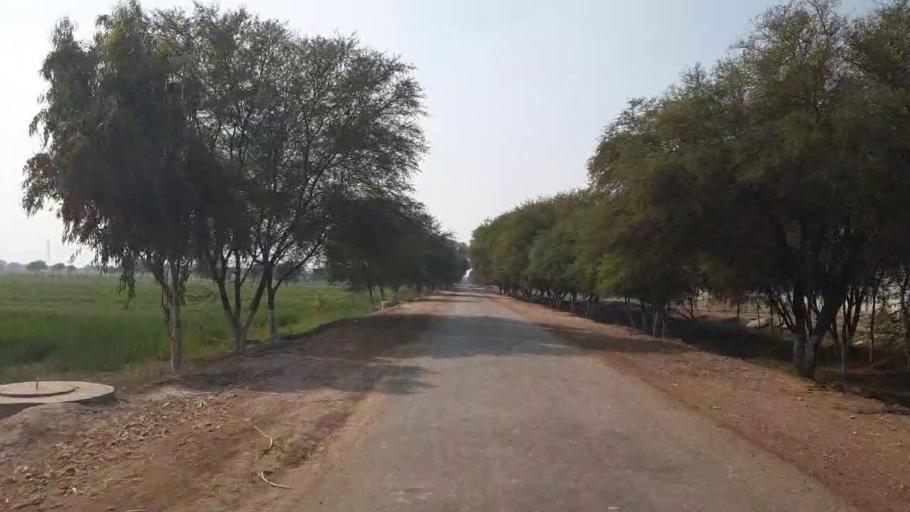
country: PK
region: Sindh
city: Mirwah Gorchani
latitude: 25.3535
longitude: 68.9389
